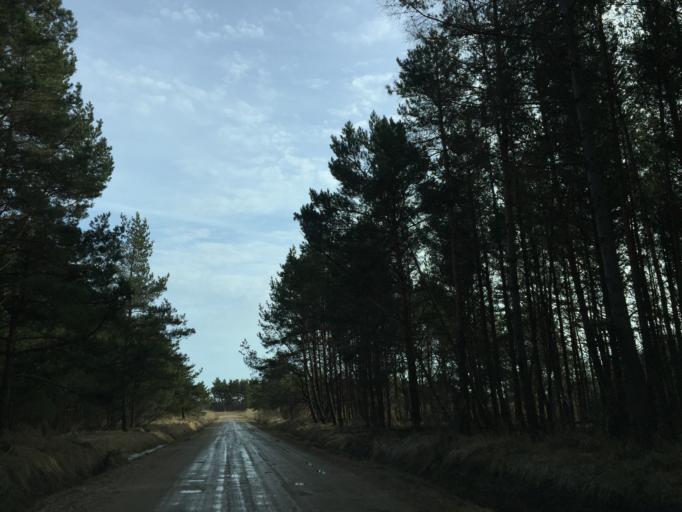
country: EE
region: Paernumaa
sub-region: Paernu linn
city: Parnu
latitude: 58.2402
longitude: 24.4837
